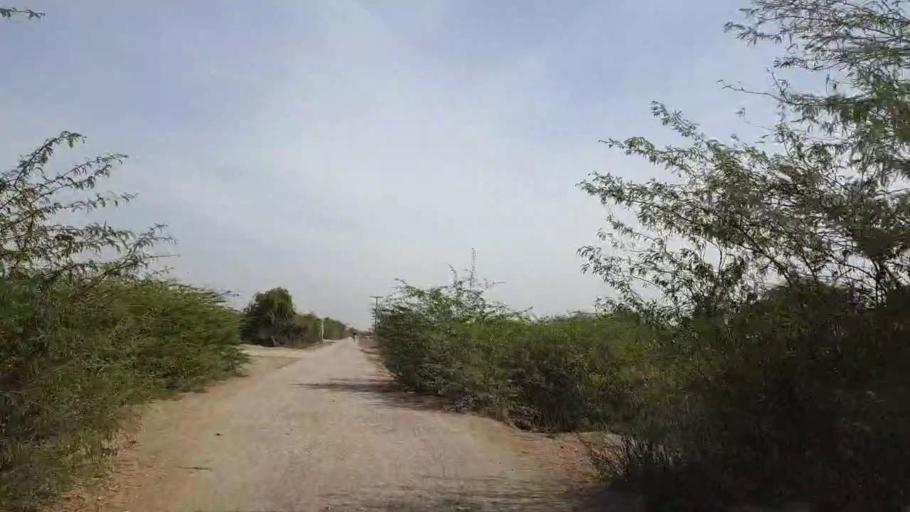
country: PK
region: Sindh
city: Kunri
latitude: 25.1767
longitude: 69.6297
